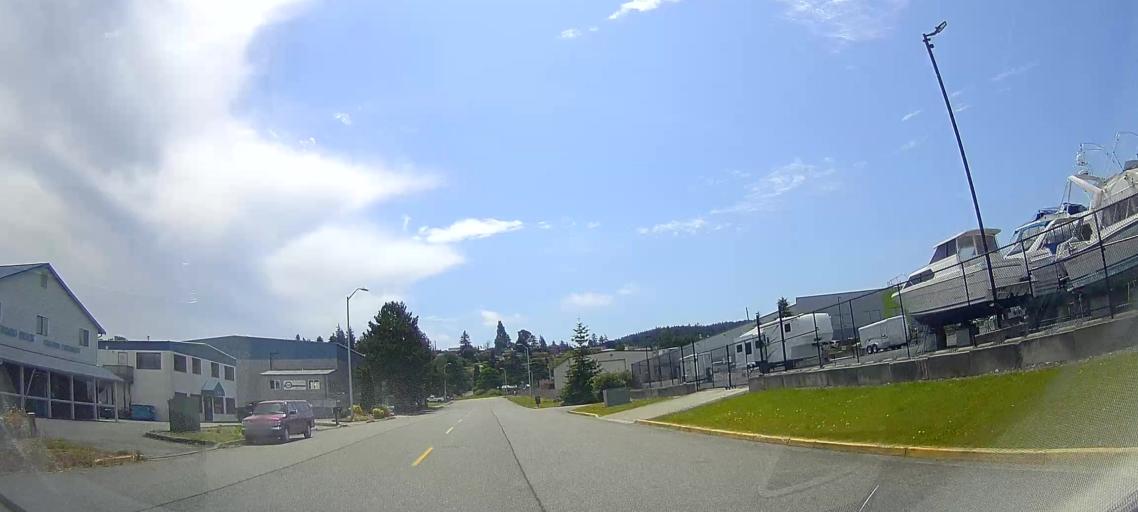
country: US
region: Washington
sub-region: Skagit County
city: Anacortes
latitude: 48.4968
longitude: -122.6067
